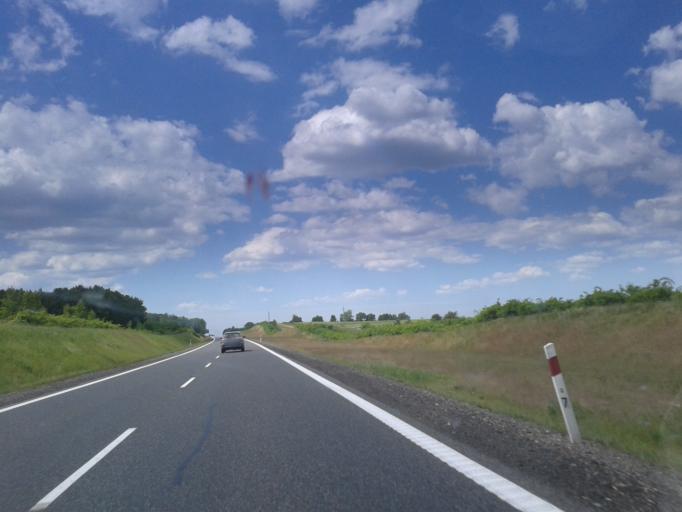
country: PL
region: Pomeranian Voivodeship
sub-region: Powiat chojnicki
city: Chojnice
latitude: 53.6830
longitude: 17.5289
